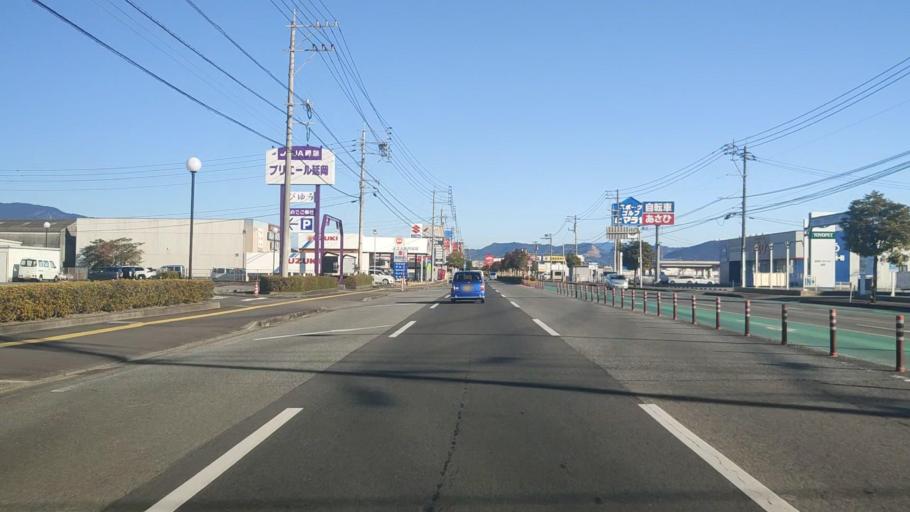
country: JP
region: Miyazaki
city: Nobeoka
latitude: 32.5629
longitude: 131.6815
